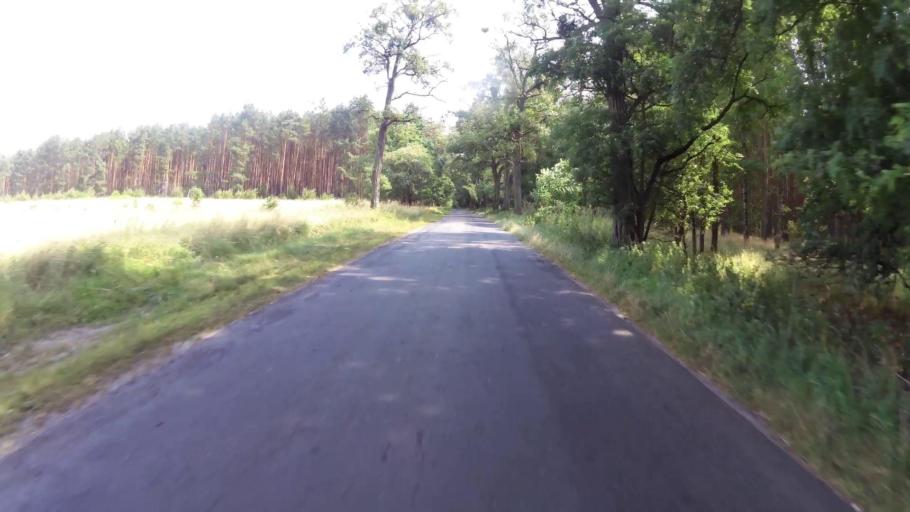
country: PL
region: West Pomeranian Voivodeship
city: Trzcinsko Zdroj
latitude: 52.8669
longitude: 14.6223
